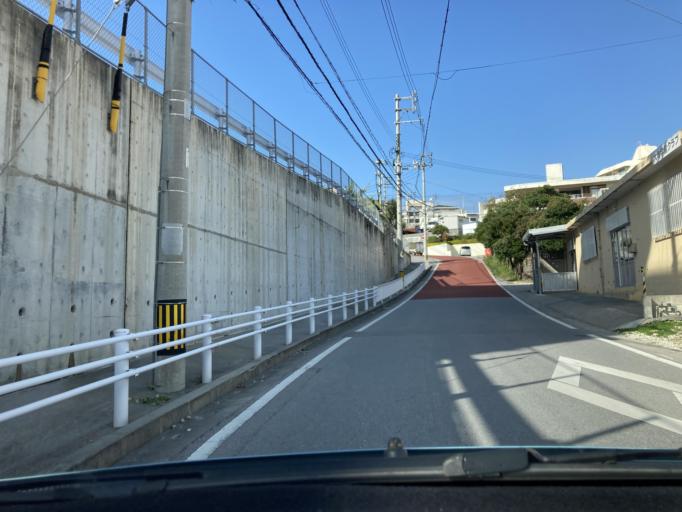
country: JP
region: Okinawa
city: Tomigusuku
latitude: 26.1814
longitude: 127.6826
